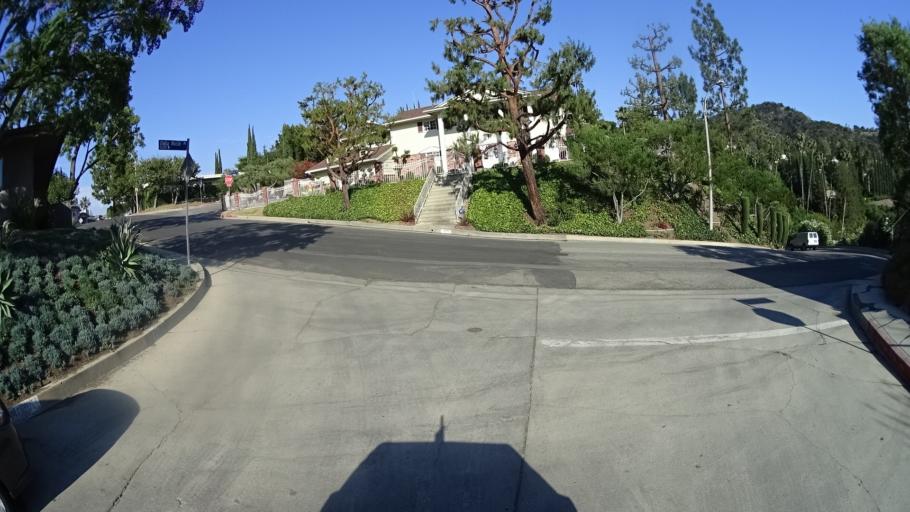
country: US
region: California
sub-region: Los Angeles County
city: Universal City
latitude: 34.1306
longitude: -118.3866
